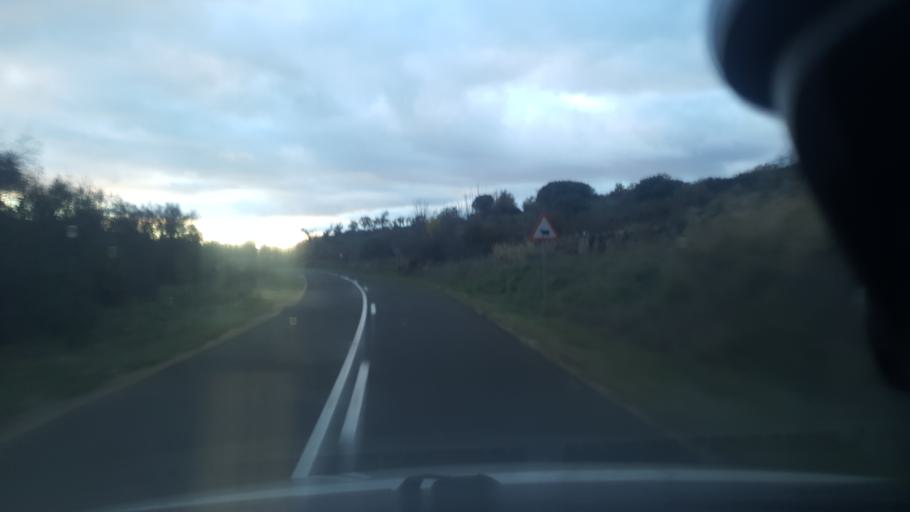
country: ES
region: Castille and Leon
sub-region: Provincia de Segovia
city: Vegas de Matute
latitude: 40.7208
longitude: -4.2999
